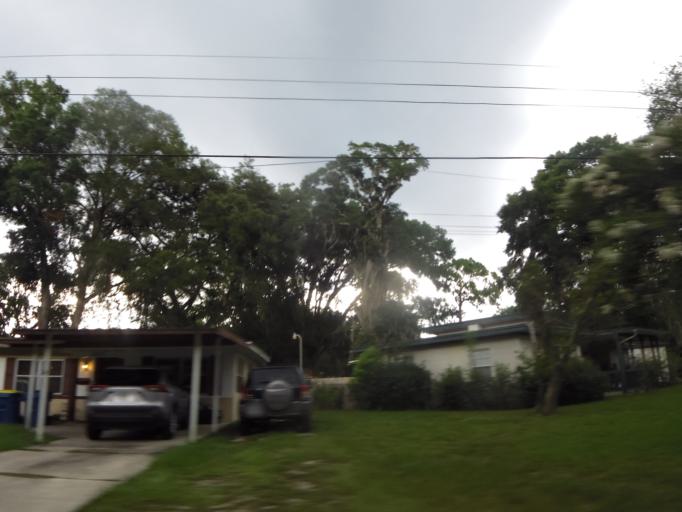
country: US
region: Florida
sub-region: Duval County
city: Jacksonville
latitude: 30.3424
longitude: -81.6052
